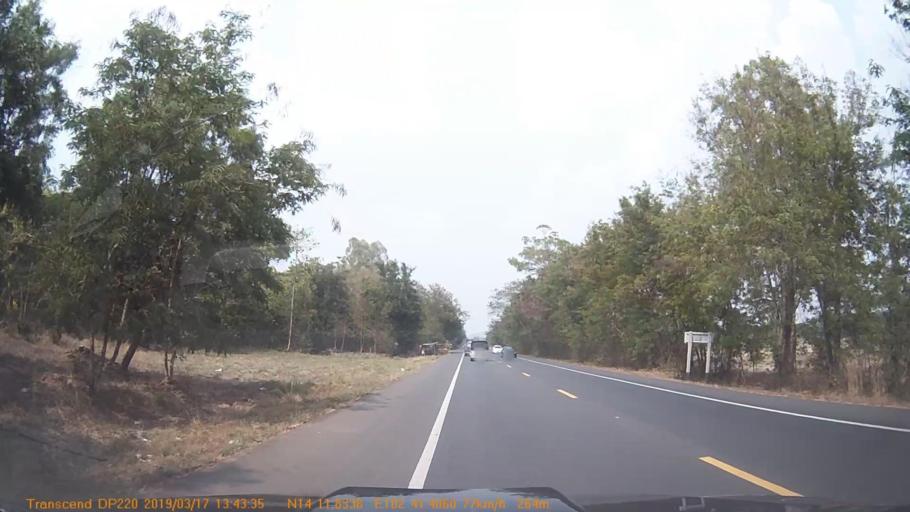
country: TH
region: Buriram
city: Non Din Daeng
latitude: 14.1976
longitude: 102.6902
